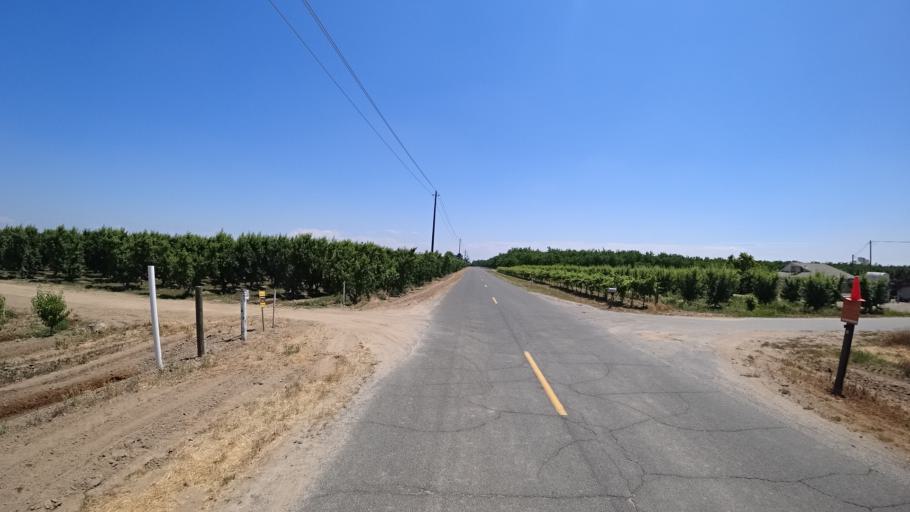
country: US
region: California
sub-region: Fresno County
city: Kingsburg
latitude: 36.4814
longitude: -119.5753
